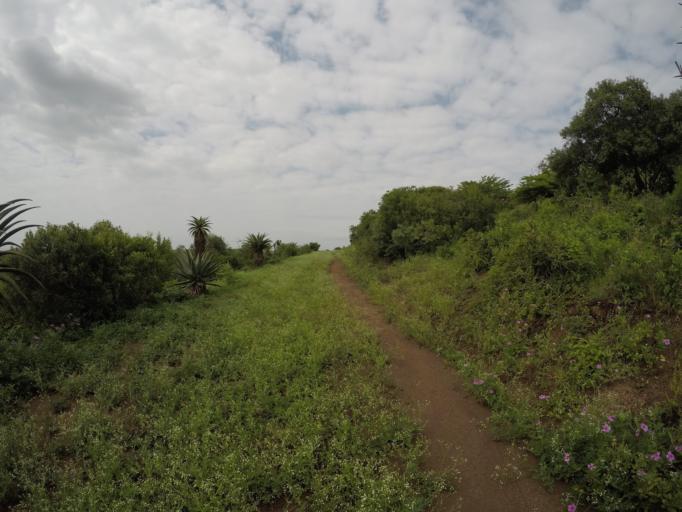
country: ZA
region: KwaZulu-Natal
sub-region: uThungulu District Municipality
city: Empangeni
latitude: -28.6319
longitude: 31.9099
